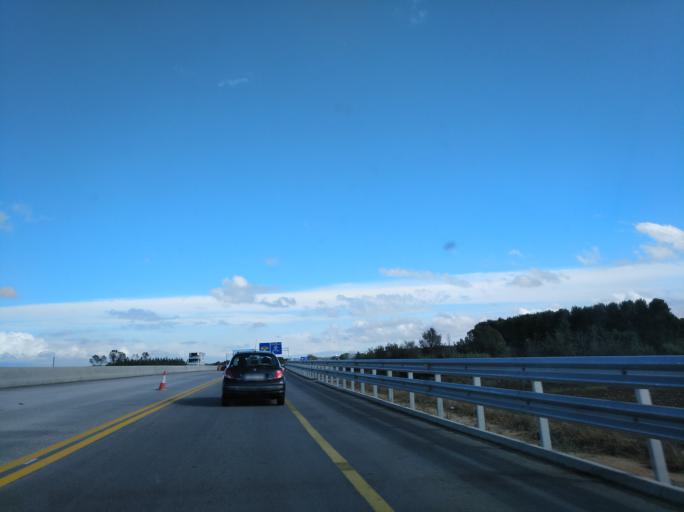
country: ES
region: Catalonia
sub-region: Provincia de Girona
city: Sils
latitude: 41.7907
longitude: 2.7573
